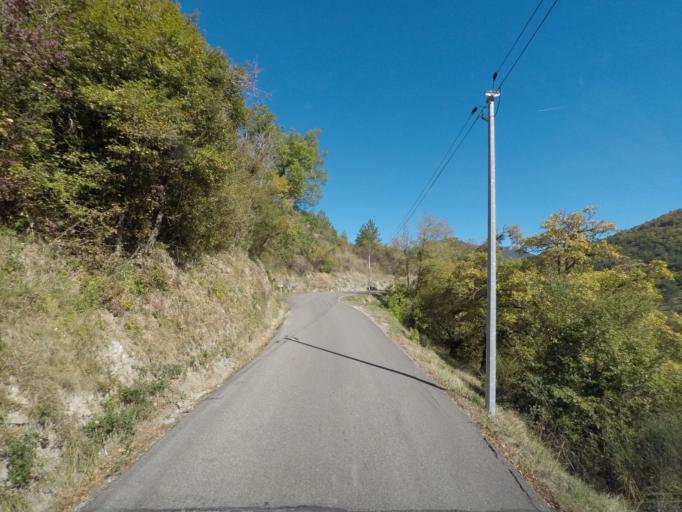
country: FR
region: Rhone-Alpes
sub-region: Departement de la Drome
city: Die
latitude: 44.6085
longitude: 5.2924
